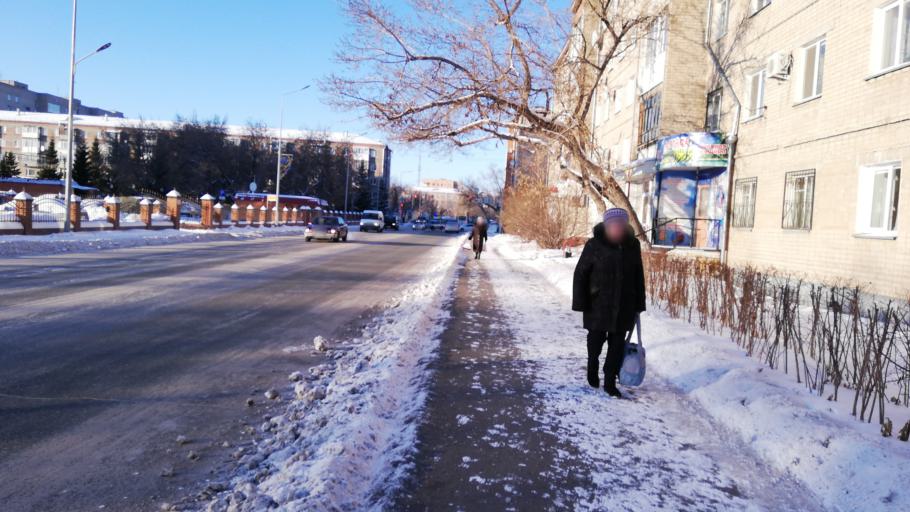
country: KZ
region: Soltustik Qazaqstan
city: Petropavlovsk
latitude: 54.8639
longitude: 69.1418
